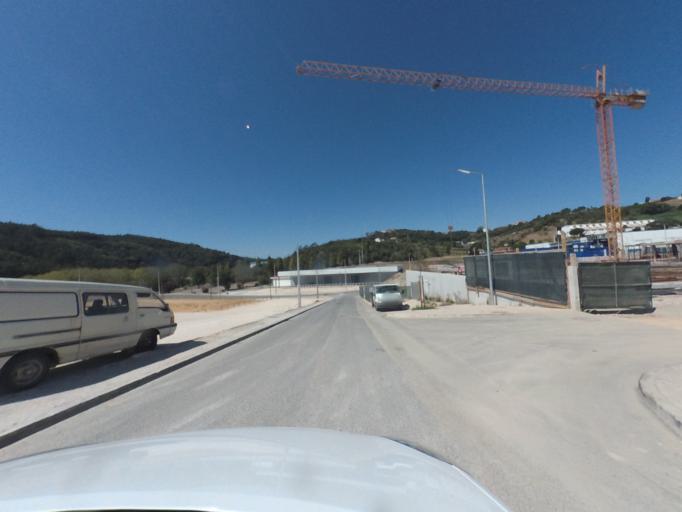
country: PT
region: Leiria
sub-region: Alcobaca
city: Alcobaca
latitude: 39.5569
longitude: -8.9784
